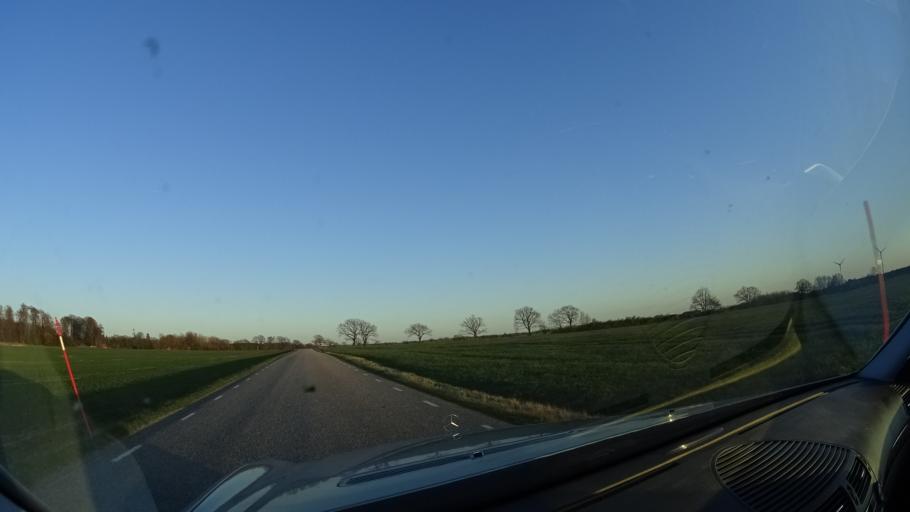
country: SE
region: Skane
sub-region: Hoors Kommun
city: Loberod
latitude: 55.8403
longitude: 13.4551
